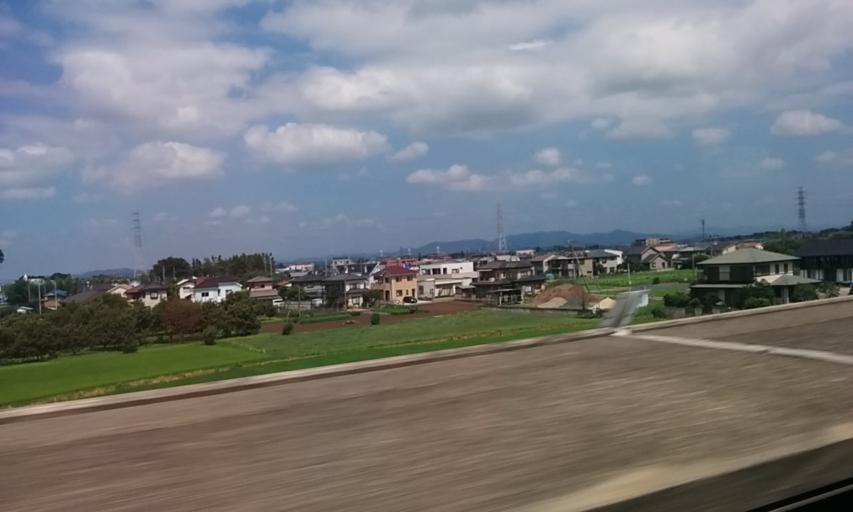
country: JP
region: Tochigi
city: Oyama
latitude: 36.2536
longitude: 139.7681
